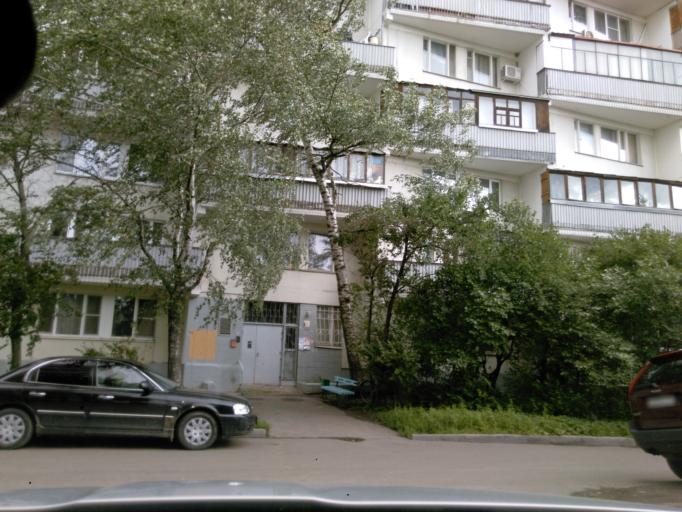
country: RU
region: Moskovskaya
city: Mendeleyevo
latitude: 56.0099
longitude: 37.2063
